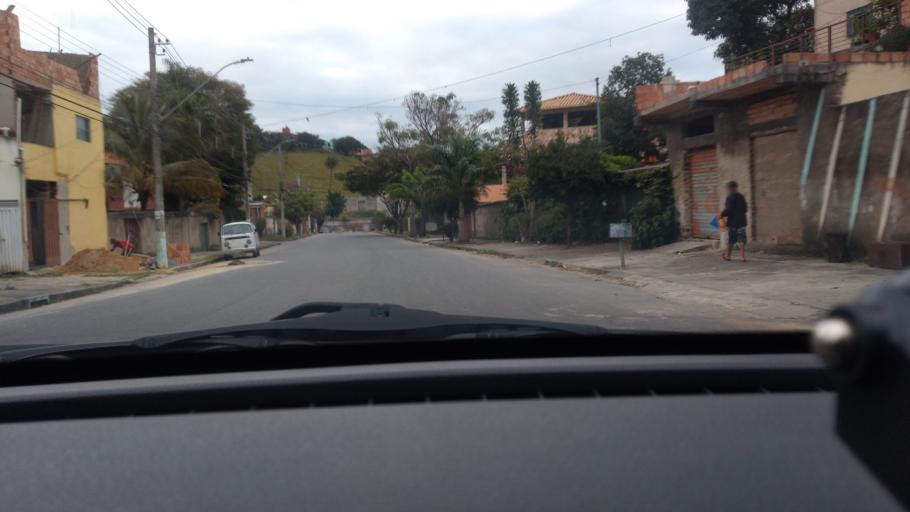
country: BR
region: Minas Gerais
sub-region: Belo Horizonte
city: Belo Horizonte
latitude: -19.8233
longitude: -43.9356
